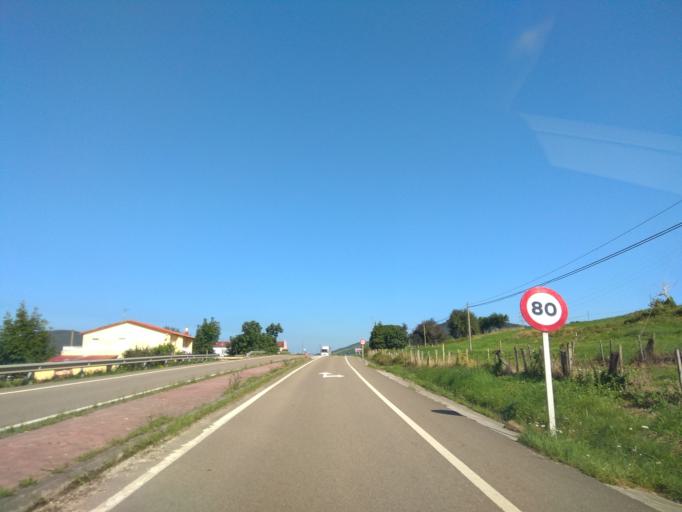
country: ES
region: Cantabria
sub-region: Provincia de Cantabria
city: Bareyo
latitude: 43.4741
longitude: -3.5970
